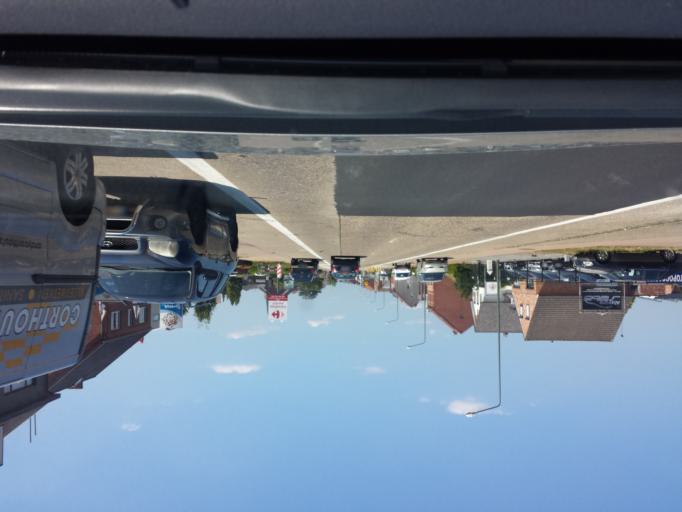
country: BE
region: Flanders
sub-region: Provincie Limburg
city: Lummen
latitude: 51.0348
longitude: 5.1643
